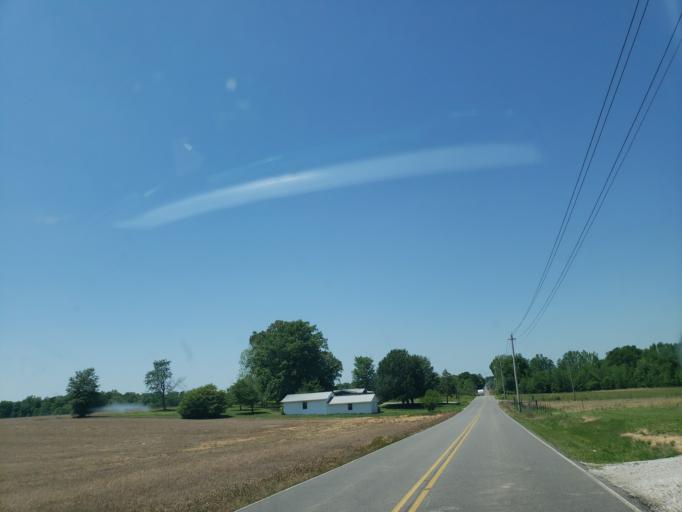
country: US
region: Alabama
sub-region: Madison County
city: Hazel Green
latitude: 34.9621
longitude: -86.6490
